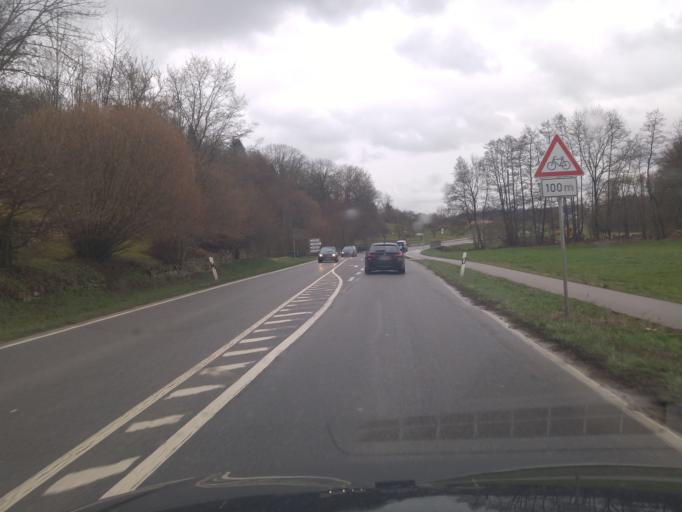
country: DE
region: Baden-Wuerttemberg
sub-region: Regierungsbezirk Stuttgart
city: Steinheim am der Murr
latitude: 48.9596
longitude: 9.2917
